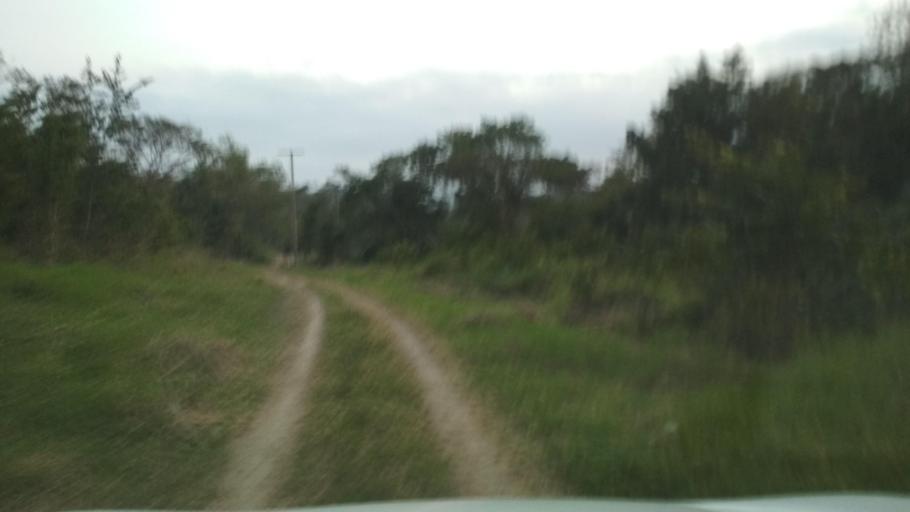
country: MX
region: Veracruz
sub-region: Poza Rica de Hidalgo
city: Arroyo del Maiz Uno
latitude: 20.4869
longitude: -97.3905
